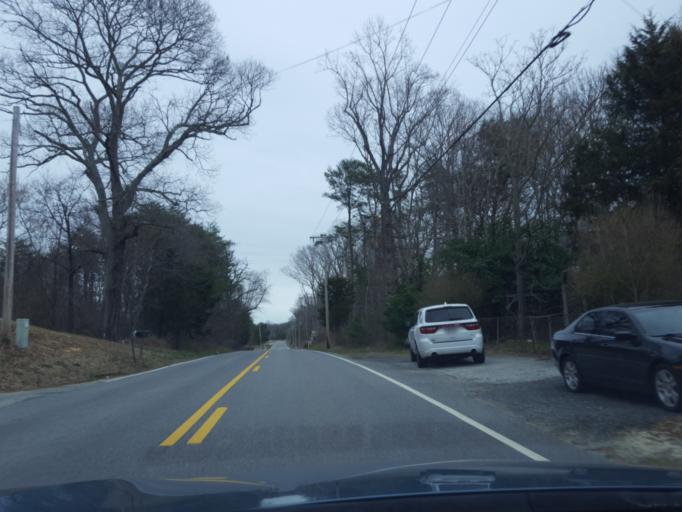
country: US
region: Maryland
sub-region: Calvert County
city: Prince Frederick
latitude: 38.5018
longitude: -76.5743
